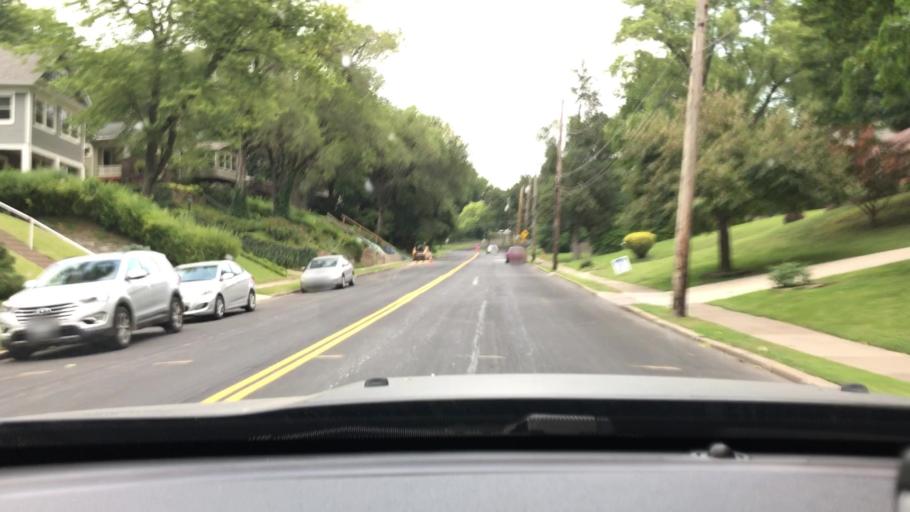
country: US
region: Iowa
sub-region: Scott County
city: Bettendorf
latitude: 41.5339
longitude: -90.5419
